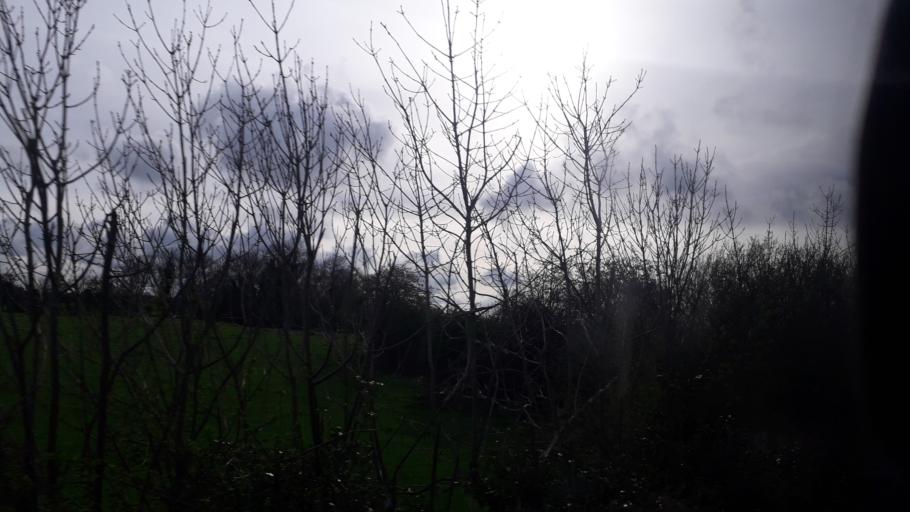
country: IE
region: Leinster
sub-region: An Mhi
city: Enfield
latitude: 53.4196
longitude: -6.8022
